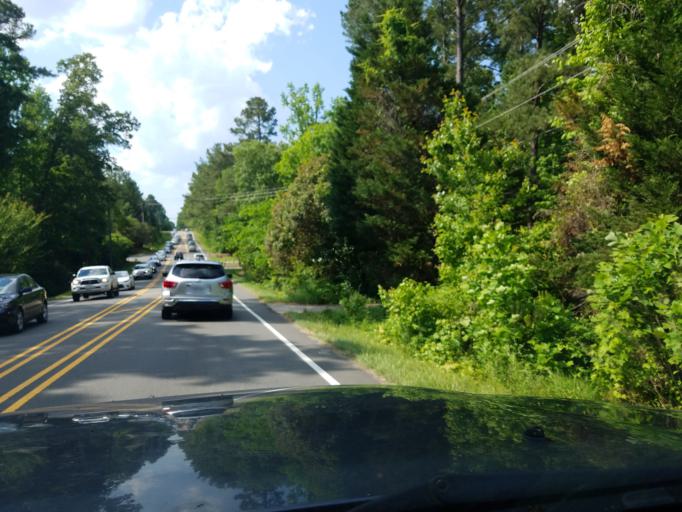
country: US
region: North Carolina
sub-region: Durham County
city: Durham
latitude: 35.9388
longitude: -78.9642
